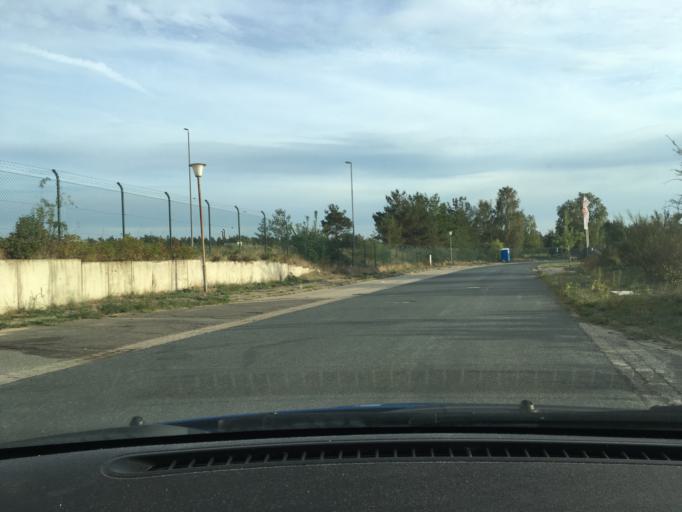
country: DE
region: Lower Saxony
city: Soltau
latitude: 52.9904
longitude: 9.9247
